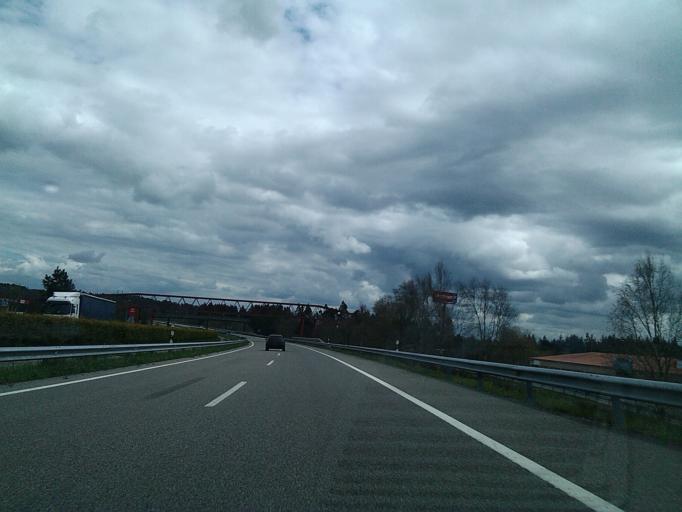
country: ES
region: Galicia
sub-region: Provincia de Lugo
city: Guitiriz
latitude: 43.1880
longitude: -7.9293
